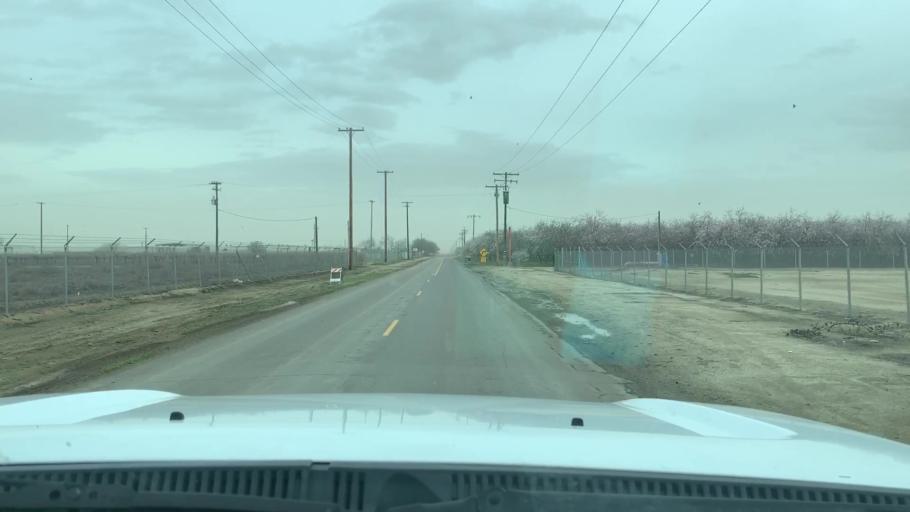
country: US
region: California
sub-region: Kern County
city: Shafter
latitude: 35.5293
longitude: -119.2633
